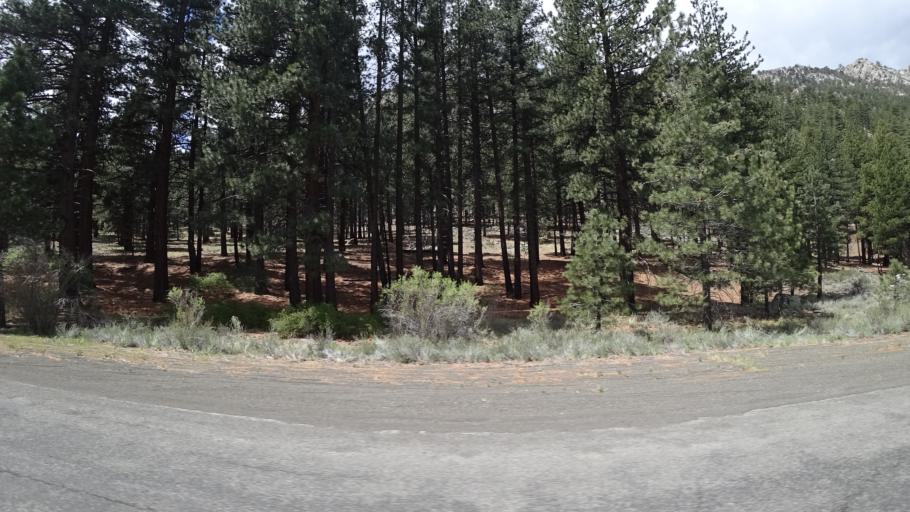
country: US
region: California
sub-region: Mono County
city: Bridgeport
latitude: 38.4475
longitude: -119.4570
